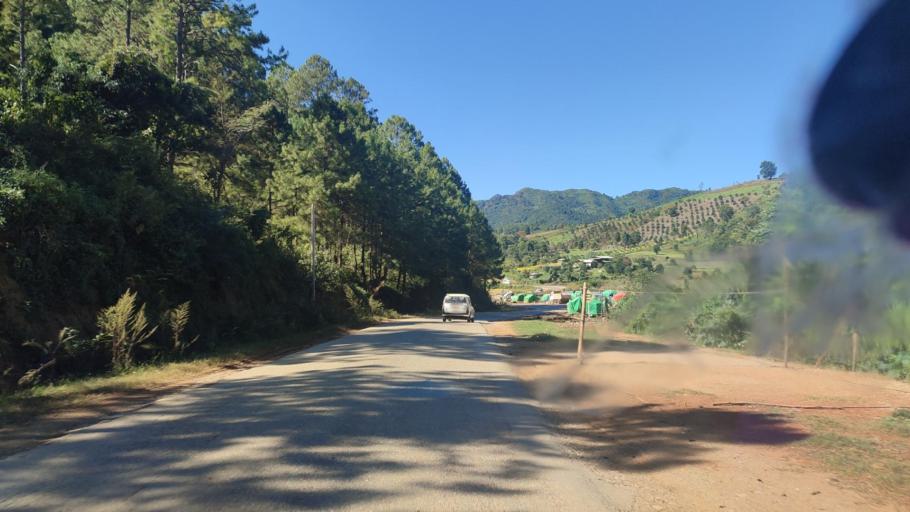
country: MM
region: Shan
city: Taunggyi
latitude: 20.8956
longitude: 97.5567
